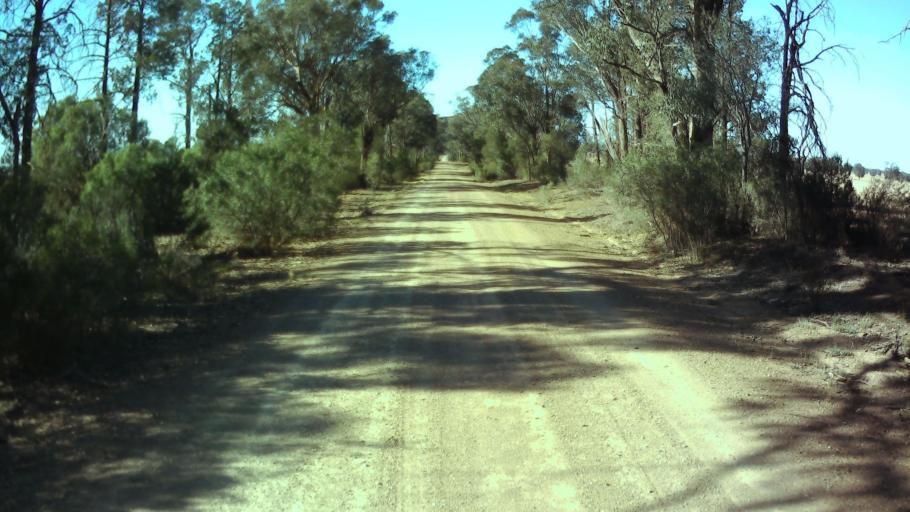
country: AU
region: New South Wales
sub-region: Weddin
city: Grenfell
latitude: -33.9108
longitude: 147.8767
